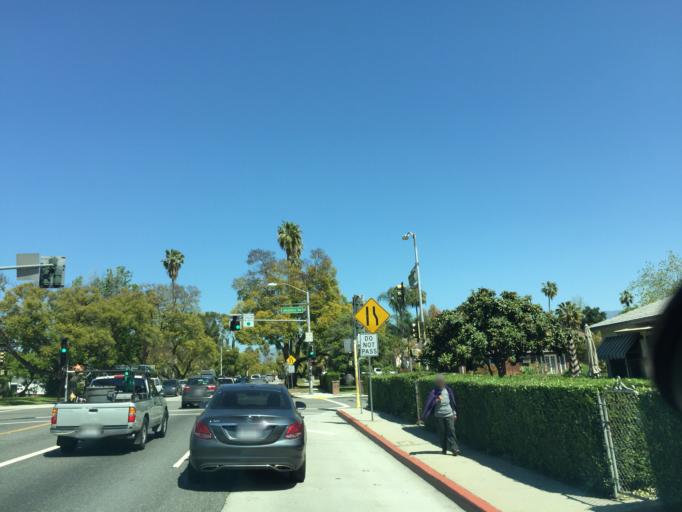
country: US
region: California
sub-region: Los Angeles County
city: South Pasadena
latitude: 34.0982
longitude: -118.1520
